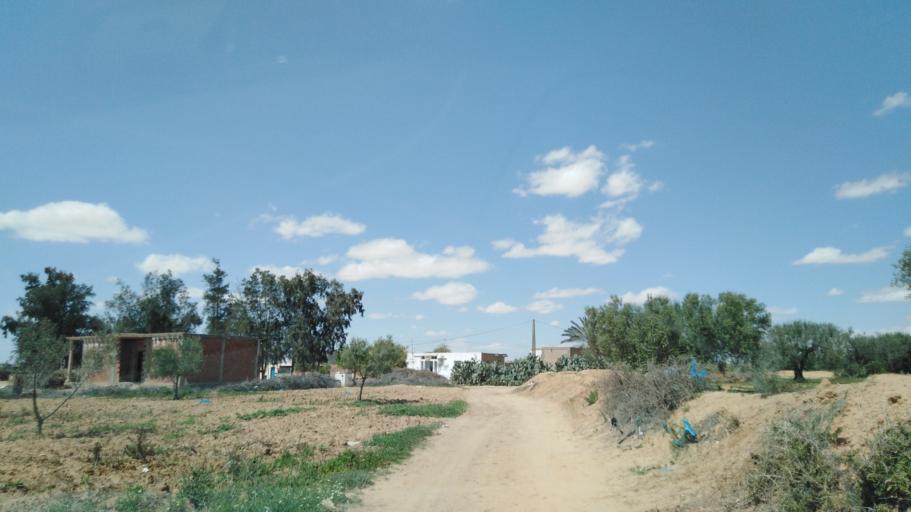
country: TN
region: Safaqis
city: Sfax
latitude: 34.7471
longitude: 10.5398
